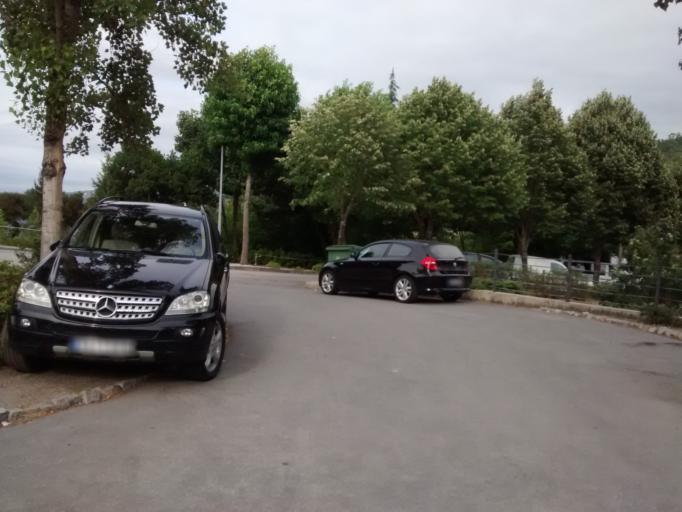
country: PT
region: Porto
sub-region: Amarante
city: Amarante
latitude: 41.2491
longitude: -8.1073
